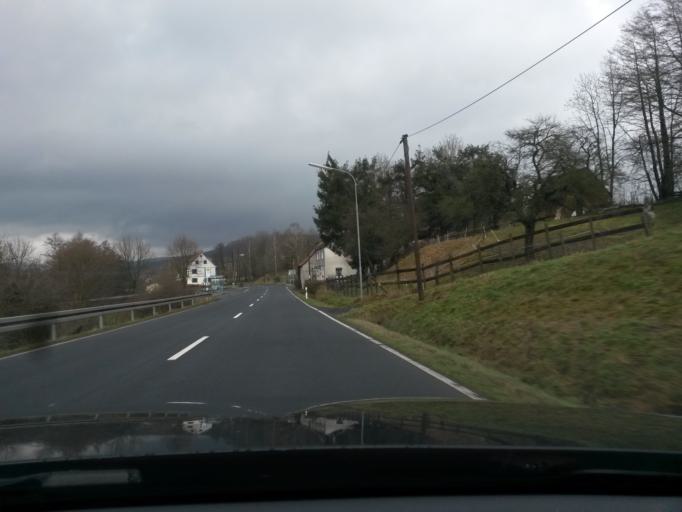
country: DE
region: Thuringia
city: Birx
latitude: 50.5119
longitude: 10.0160
